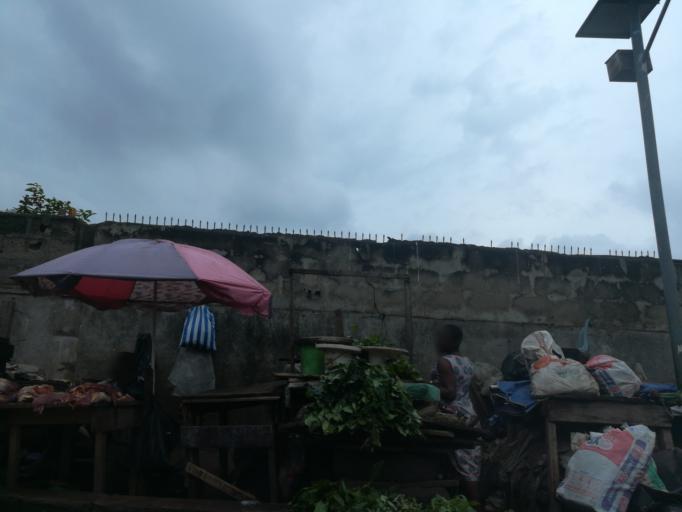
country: NG
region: Lagos
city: Ojota
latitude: 6.5724
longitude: 3.3697
